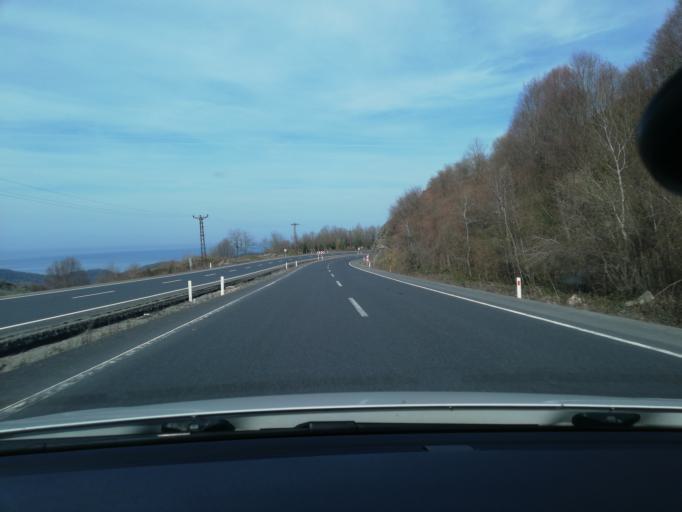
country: TR
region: Zonguldak
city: Eregli
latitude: 41.3298
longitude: 31.5734
